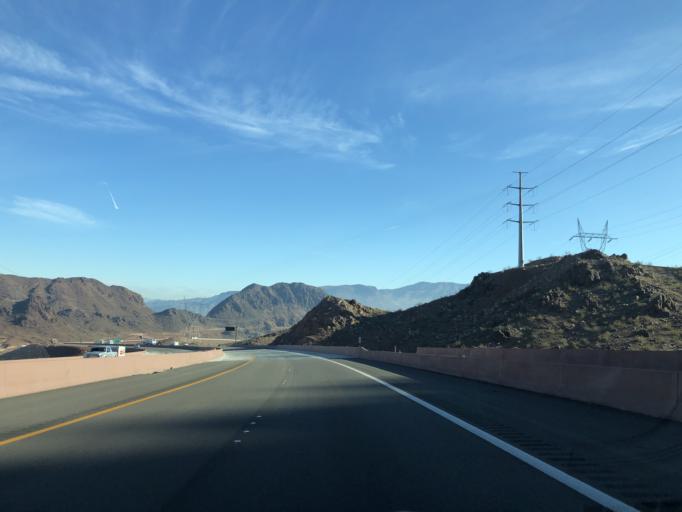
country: US
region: Nevada
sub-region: Clark County
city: Boulder City
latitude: 36.0036
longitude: -114.7842
